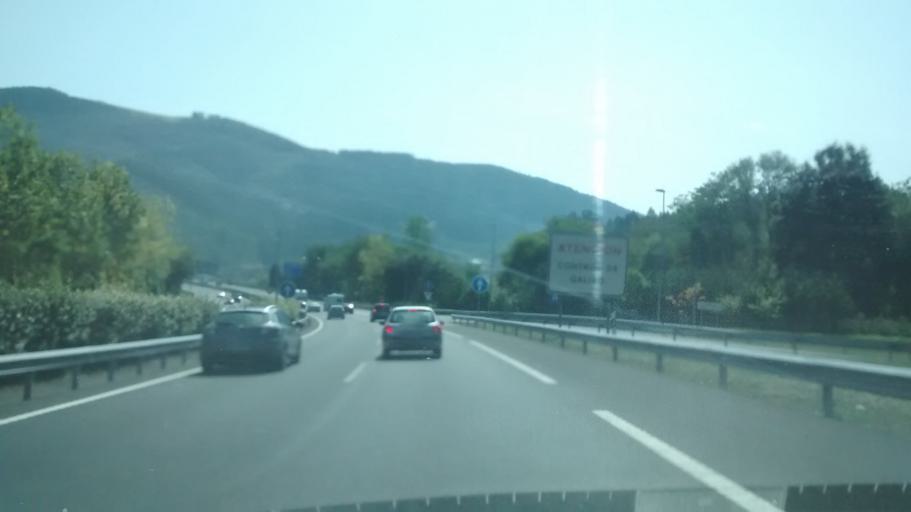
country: ES
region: Cantabria
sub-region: Provincia de Cantabria
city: Liendo
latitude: 43.3862
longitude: -3.3271
